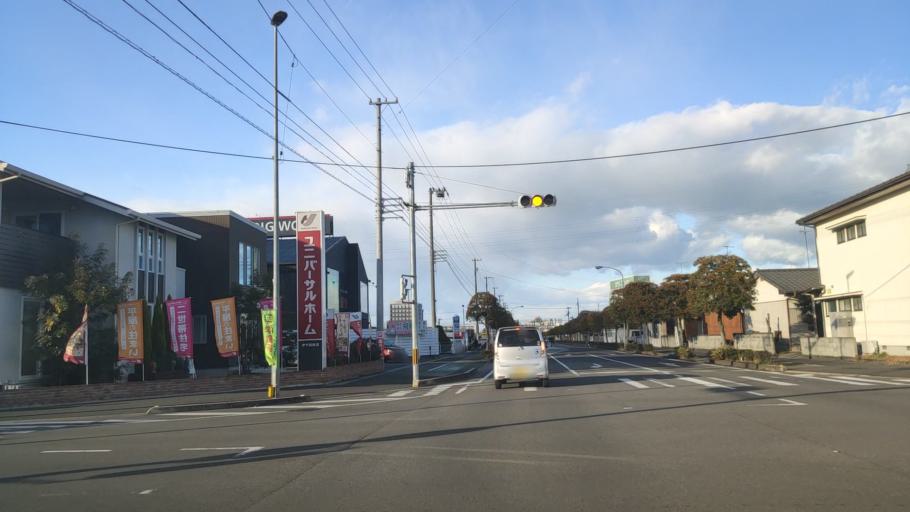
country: JP
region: Ehime
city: Saijo
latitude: 33.9240
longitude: 133.1839
